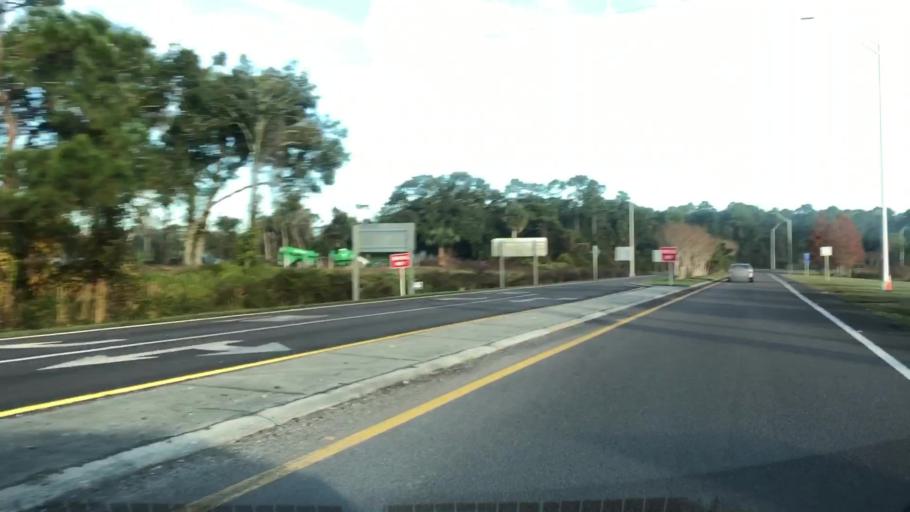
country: US
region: Florida
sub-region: Volusia County
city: DeBary
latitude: 28.8719
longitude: -81.2853
